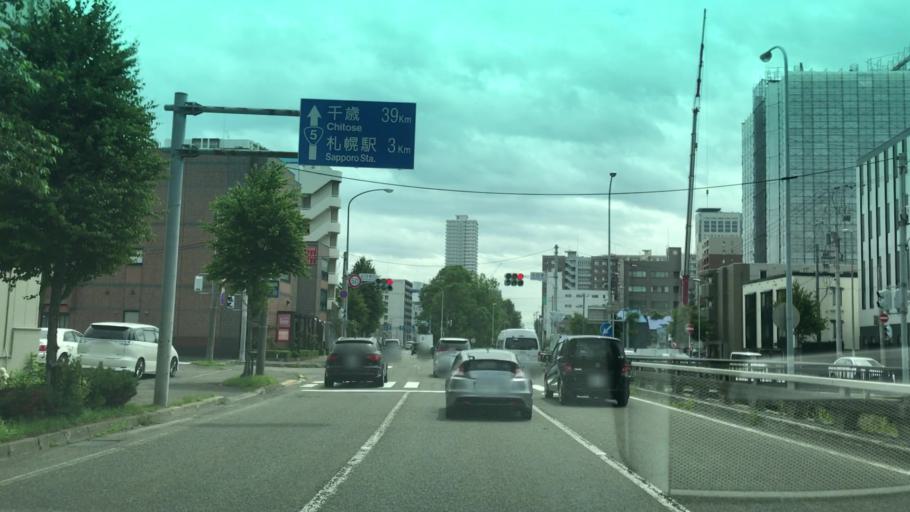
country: JP
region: Hokkaido
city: Sapporo
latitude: 43.0780
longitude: 141.3524
